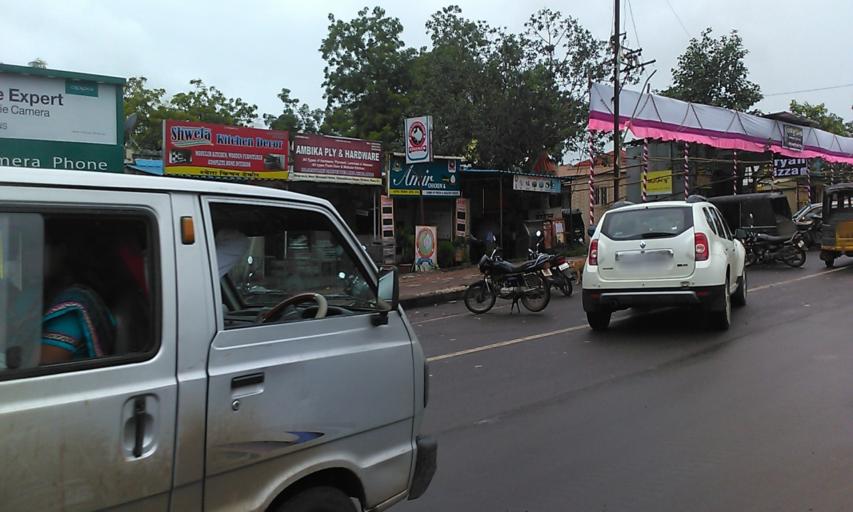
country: IN
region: Maharashtra
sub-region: Pune Division
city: Shivaji Nagar
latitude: 18.5427
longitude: 73.7895
